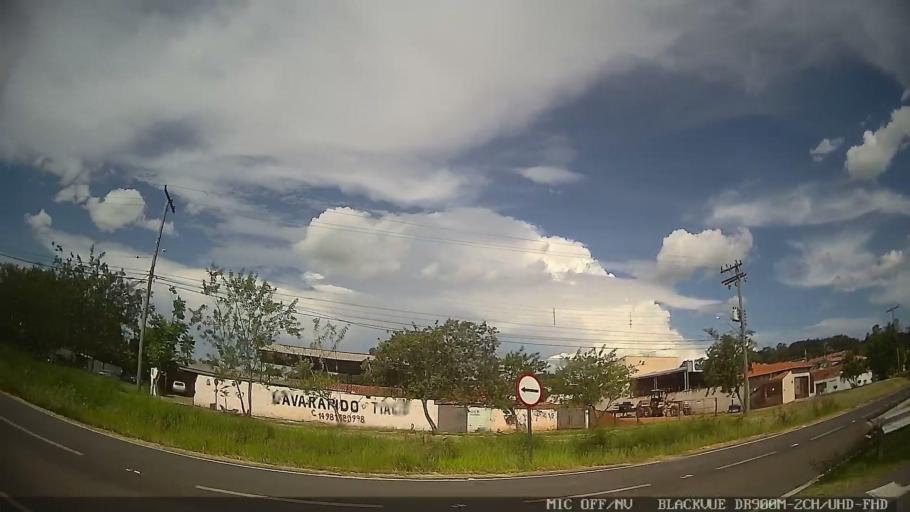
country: BR
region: Sao Paulo
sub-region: Conchas
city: Conchas
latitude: -23.0697
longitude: -47.9733
